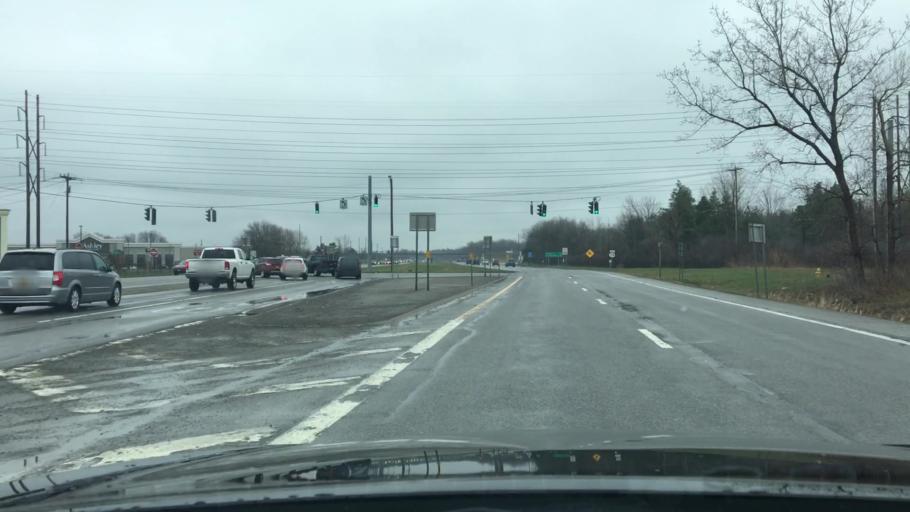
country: US
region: New York
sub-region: Erie County
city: Blasdell
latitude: 42.7891
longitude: -78.7831
